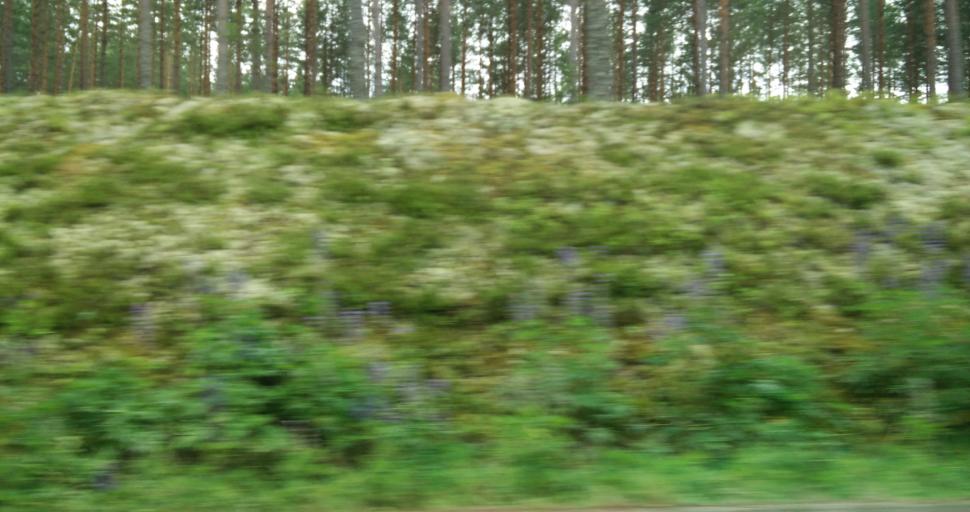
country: SE
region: Vaermland
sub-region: Munkfors Kommun
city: Munkfors
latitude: 59.9683
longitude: 13.4966
